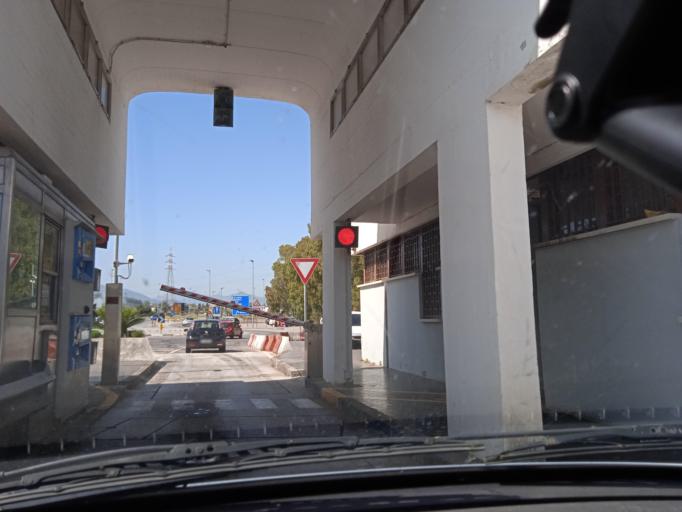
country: IT
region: Sicily
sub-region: Messina
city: San Filippo del Mela
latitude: 38.1898
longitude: 15.2742
